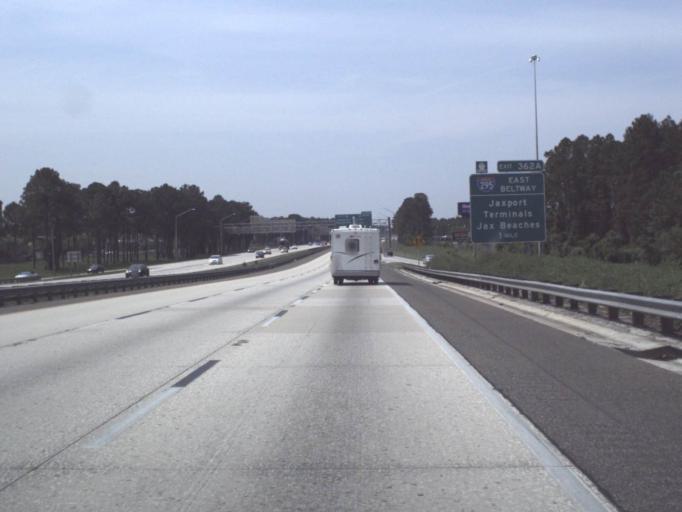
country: US
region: Florida
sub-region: Duval County
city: Jacksonville
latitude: 30.4800
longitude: -81.6442
